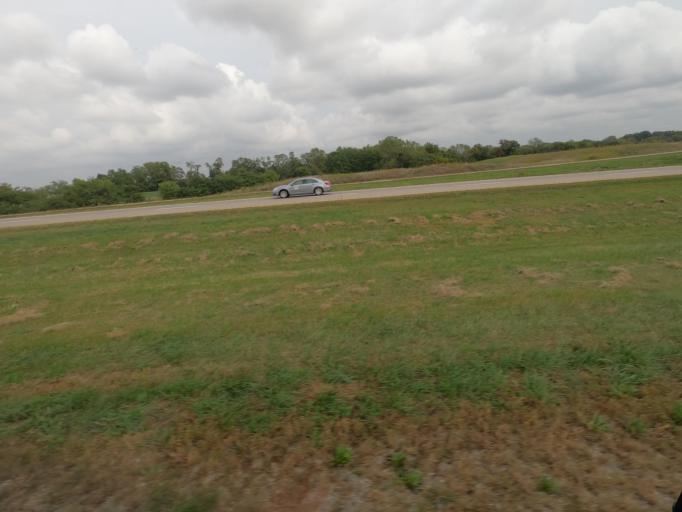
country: US
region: Iowa
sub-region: Wapello County
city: Ottumwa
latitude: 41.0532
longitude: -92.3734
